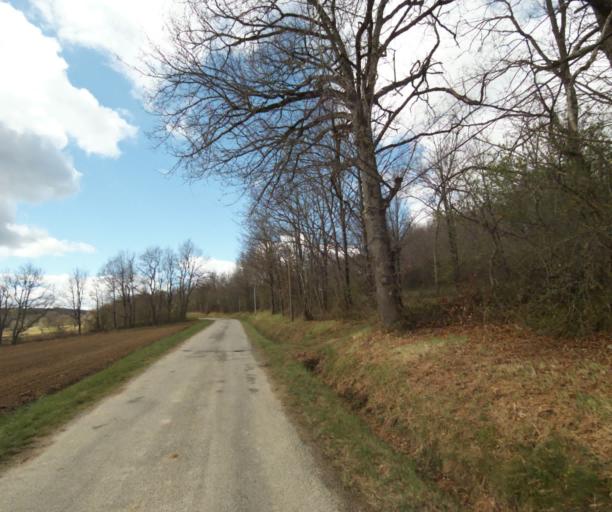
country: FR
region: Midi-Pyrenees
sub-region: Departement de l'Ariege
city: Saverdun
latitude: 43.1991
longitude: 1.5686
